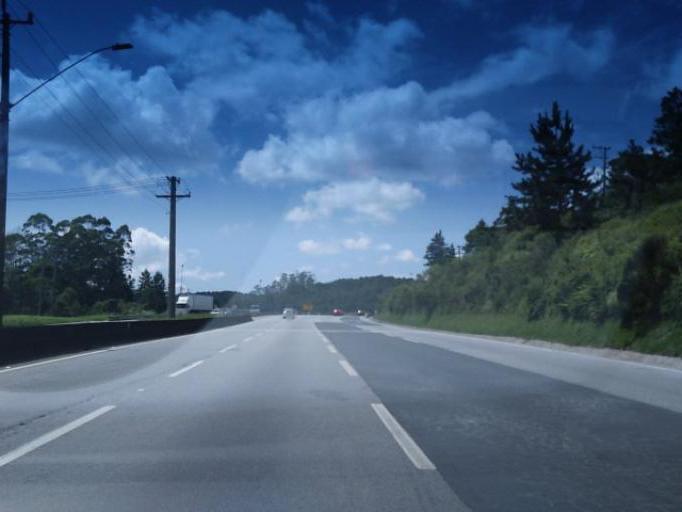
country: BR
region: Sao Paulo
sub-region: Sao Lourenco Da Serra
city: Sao Lourenco da Serra
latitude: -23.7837
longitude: -46.9145
